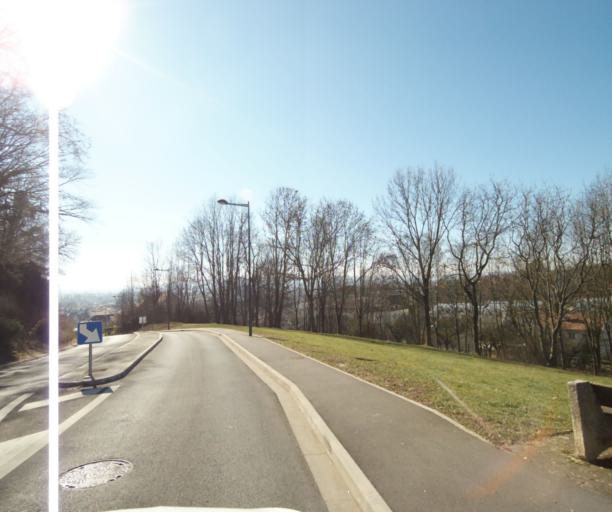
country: FR
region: Lorraine
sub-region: Departement de Meurthe-et-Moselle
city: Essey-les-Nancy
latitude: 48.7091
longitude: 6.2196
